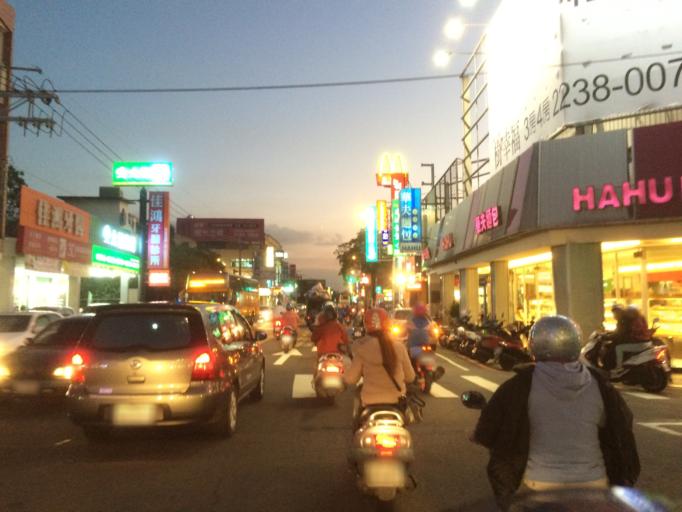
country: TW
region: Taiwan
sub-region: Taichung City
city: Taichung
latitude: 24.1758
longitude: 120.7191
